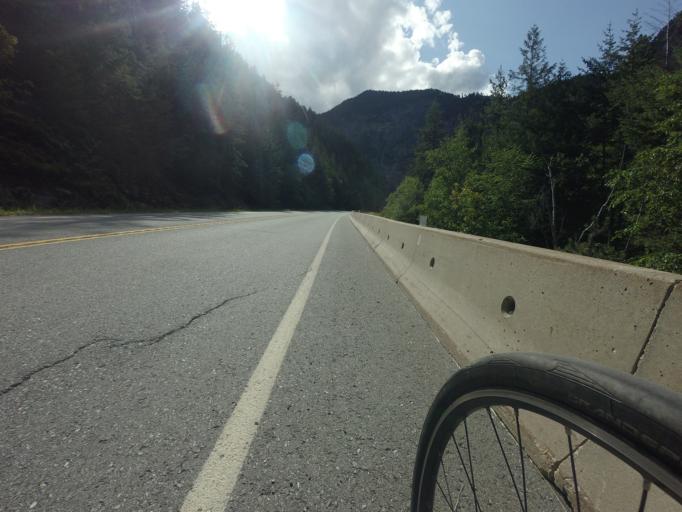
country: CA
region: British Columbia
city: Lillooet
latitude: 50.6452
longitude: -122.0602
